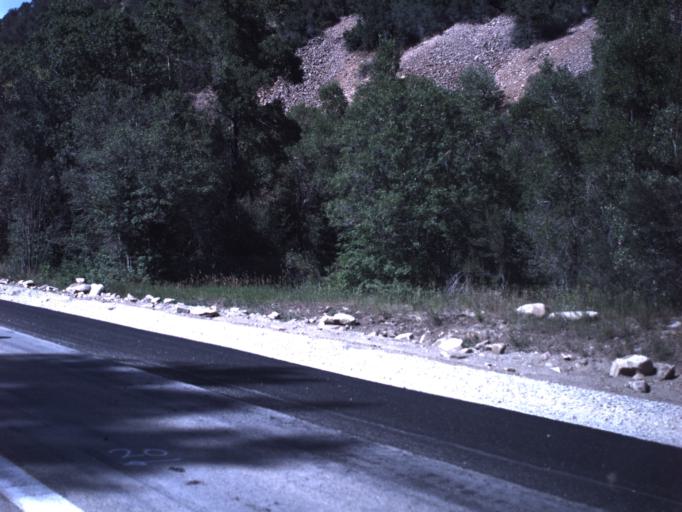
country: US
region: Utah
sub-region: Wasatch County
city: Heber
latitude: 40.3606
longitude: -111.2851
